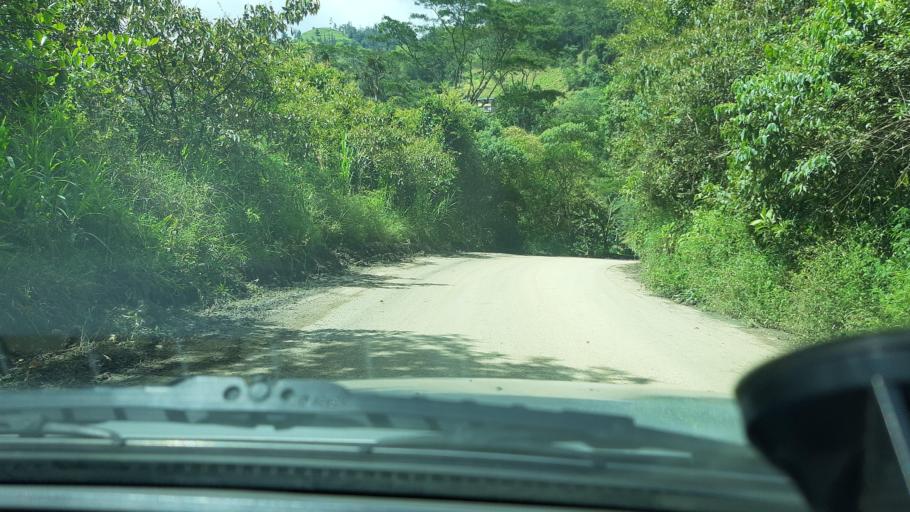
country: CO
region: Boyaca
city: Chinavita
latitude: 5.1832
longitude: -73.3832
